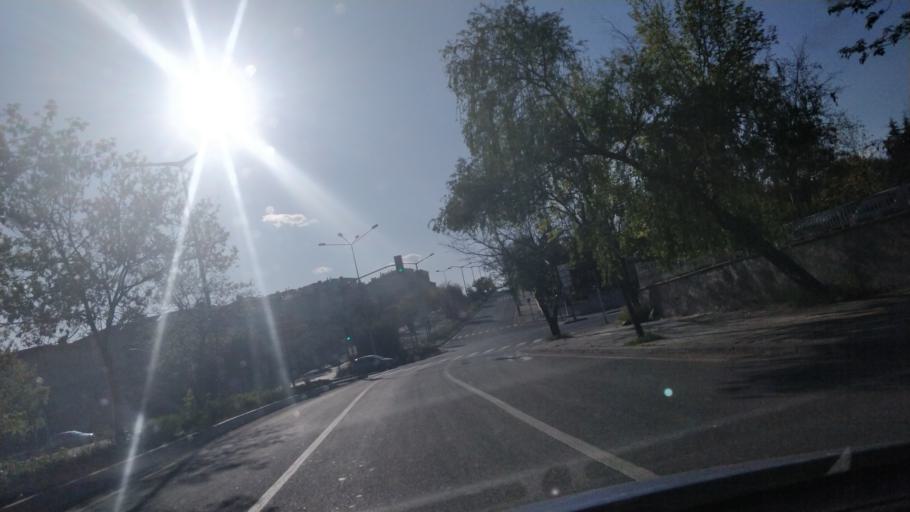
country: TR
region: Ankara
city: Batikent
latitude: 39.9580
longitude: 32.7214
